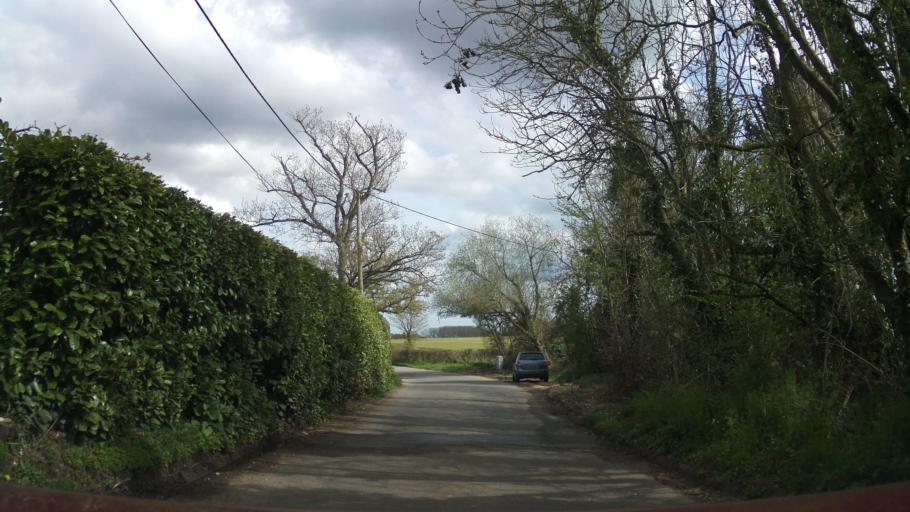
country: GB
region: England
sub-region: Hampshire
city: Romsey
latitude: 51.0301
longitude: -1.5026
